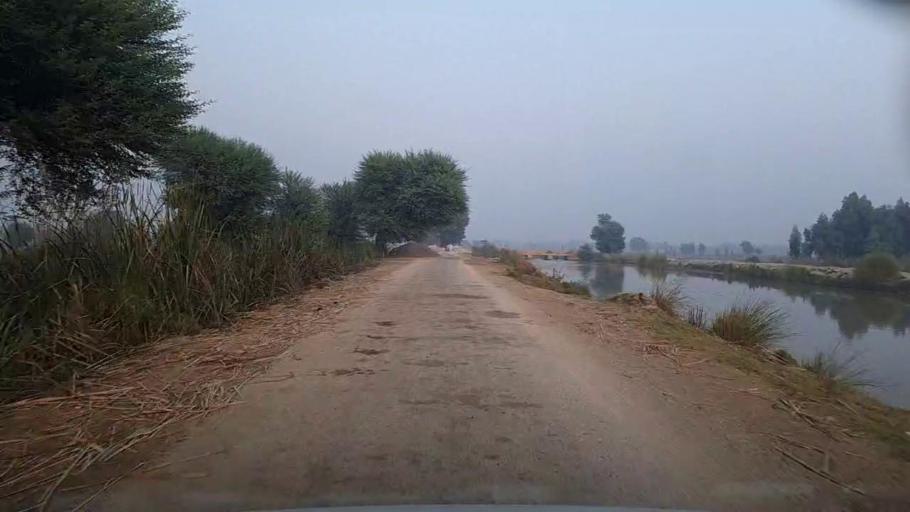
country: PK
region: Sindh
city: Kandiari
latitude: 27.0353
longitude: 68.5730
